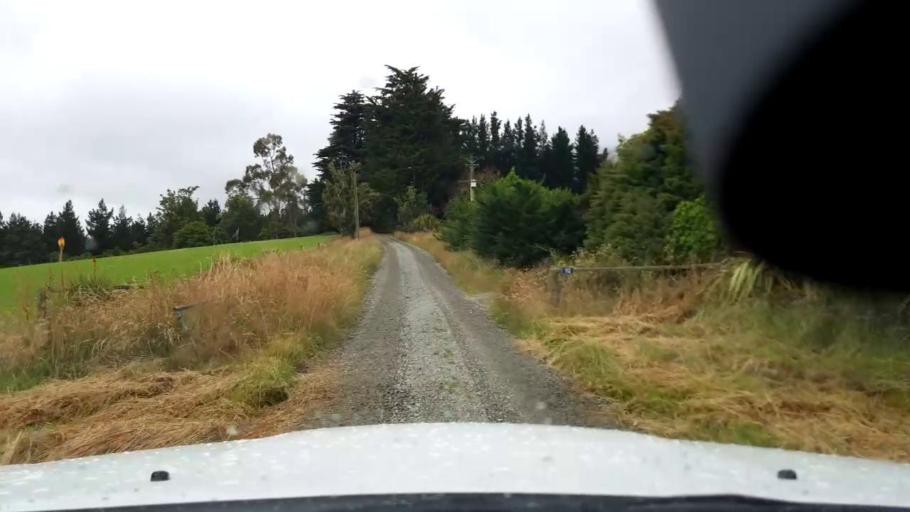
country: NZ
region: Canterbury
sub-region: Timaru District
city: Pleasant Point
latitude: -44.0774
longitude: 171.1401
